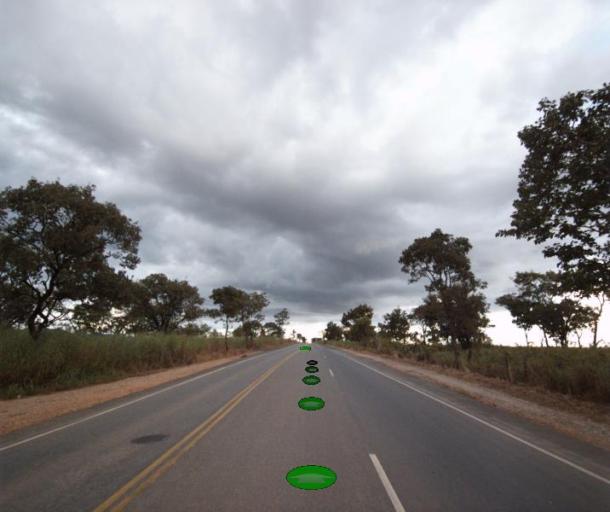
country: BR
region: Goias
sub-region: Uruacu
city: Uruacu
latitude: -14.7140
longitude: -49.2274
